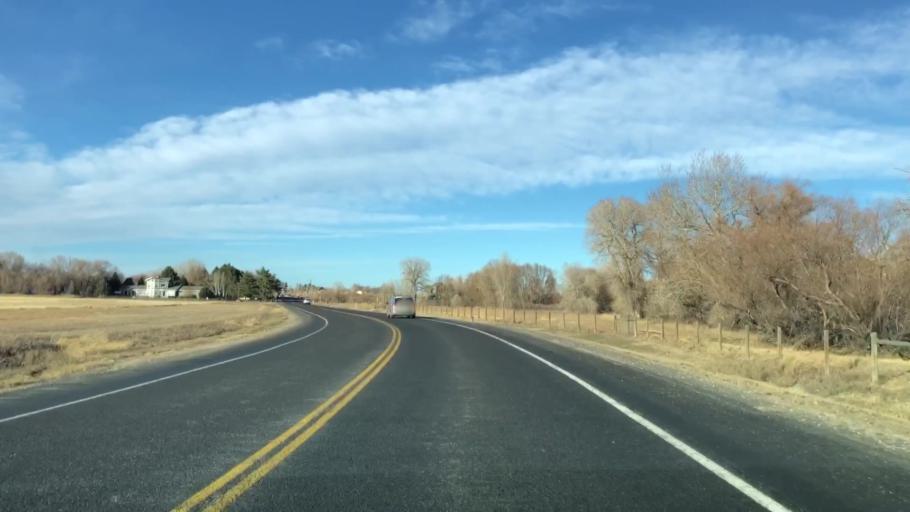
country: US
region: Colorado
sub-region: Weld County
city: Windsor
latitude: 40.5181
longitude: -104.9819
